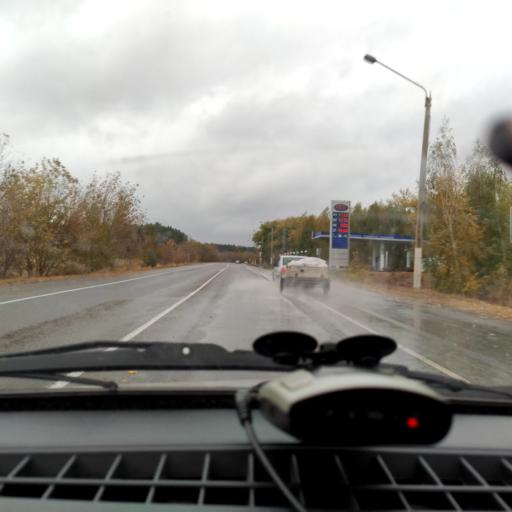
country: RU
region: Voronezj
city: Devitsa
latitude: 51.5960
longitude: 38.9764
